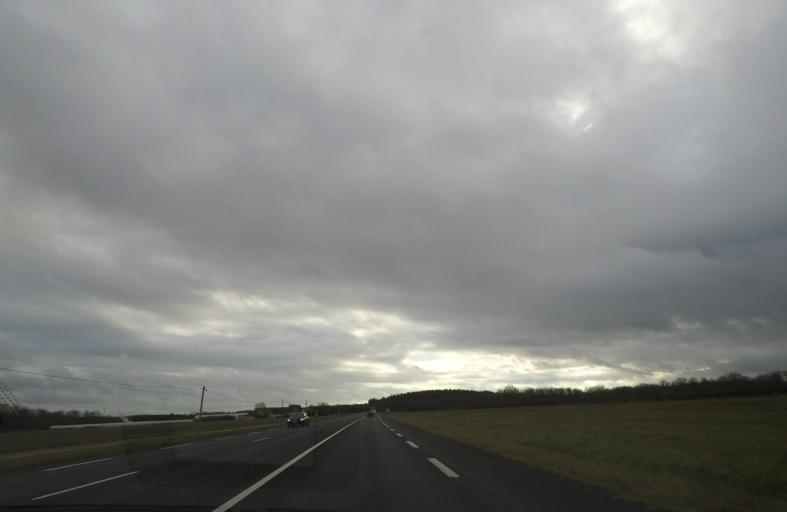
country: FR
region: Centre
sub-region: Departement du Loir-et-Cher
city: Soings-en-Sologne
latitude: 47.4433
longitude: 1.5436
